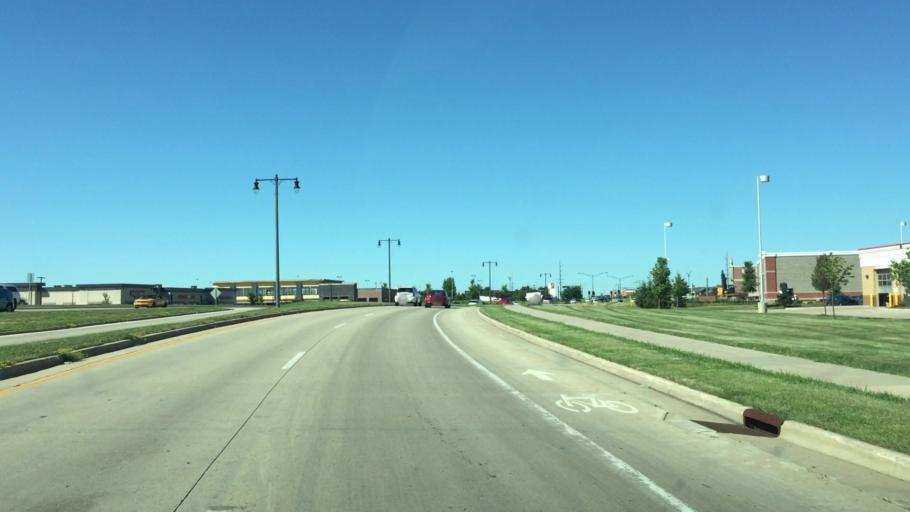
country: US
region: Wisconsin
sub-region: Dane County
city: Sun Prairie
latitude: 43.1664
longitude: -89.2688
